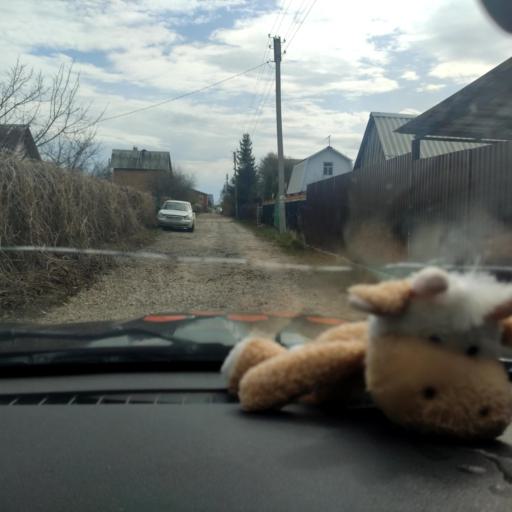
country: RU
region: Samara
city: Tol'yatti
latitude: 53.6012
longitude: 49.2417
